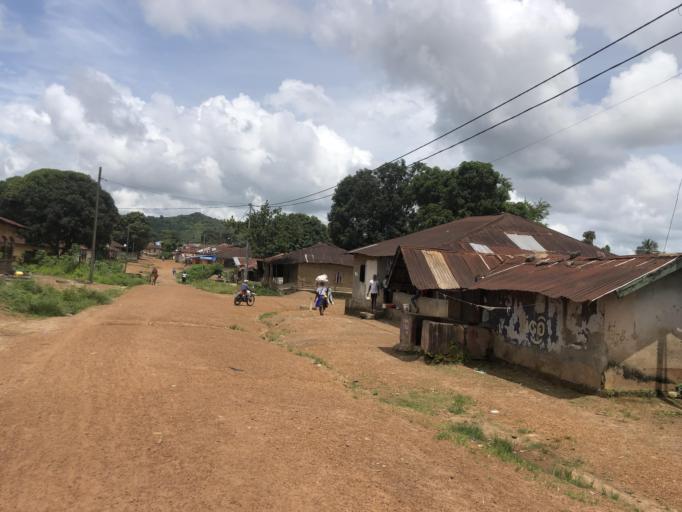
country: SL
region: Northern Province
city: Makeni
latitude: 8.8802
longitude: -12.0498
